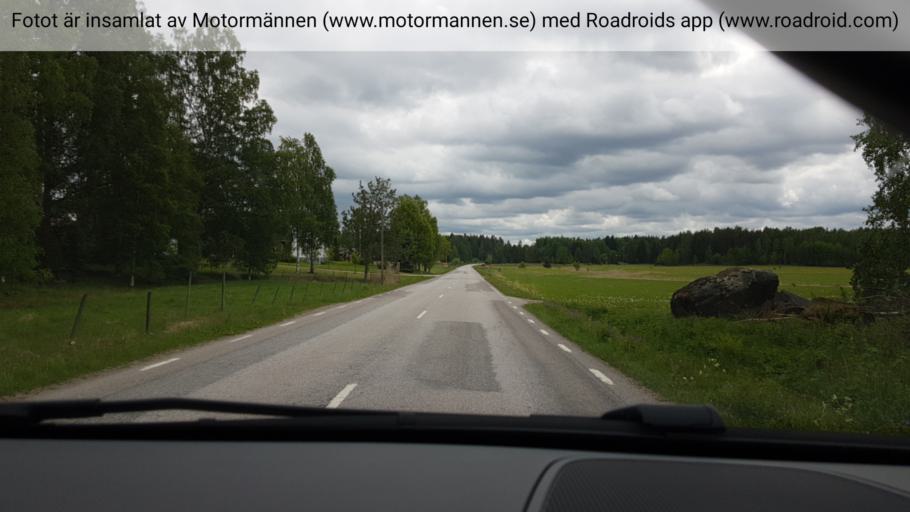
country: SE
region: Uppsala
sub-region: Heby Kommun
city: Tarnsjo
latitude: 60.1152
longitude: 17.0309
